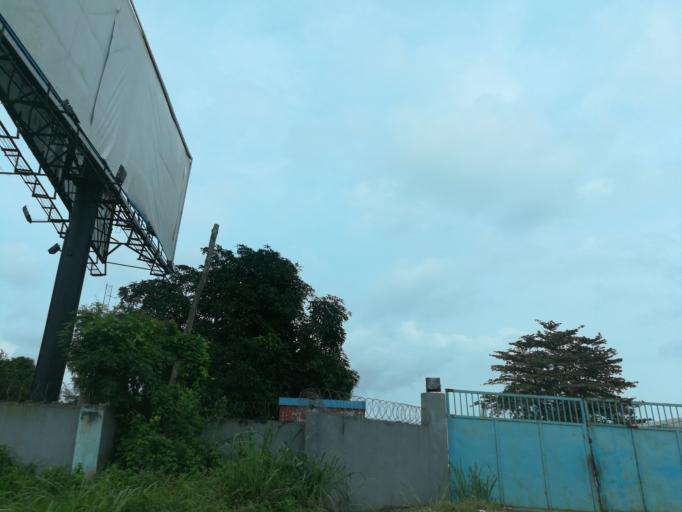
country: NG
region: Lagos
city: Oshodi
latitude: 6.5779
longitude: 3.3340
